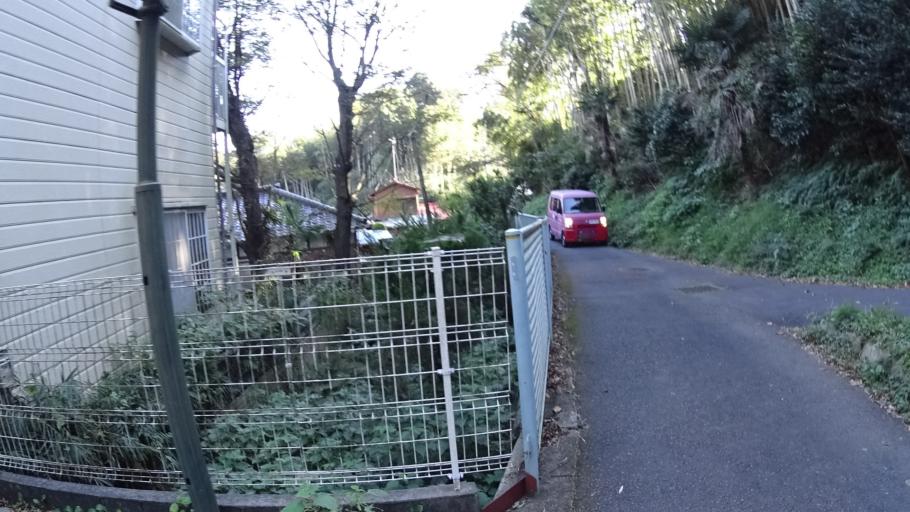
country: JP
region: Kanagawa
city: Kamakura
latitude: 35.3679
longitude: 139.5995
